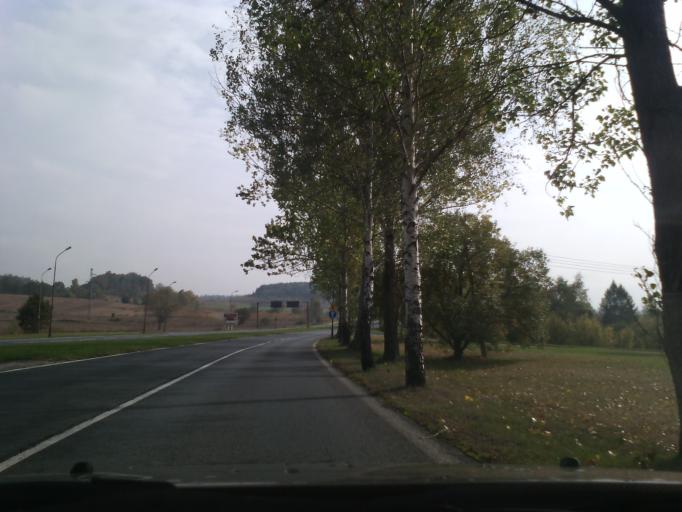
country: PL
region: Lower Silesian Voivodeship
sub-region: Powiat jeleniogorski
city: Jezow Sudecki
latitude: 50.9199
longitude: 15.7657
